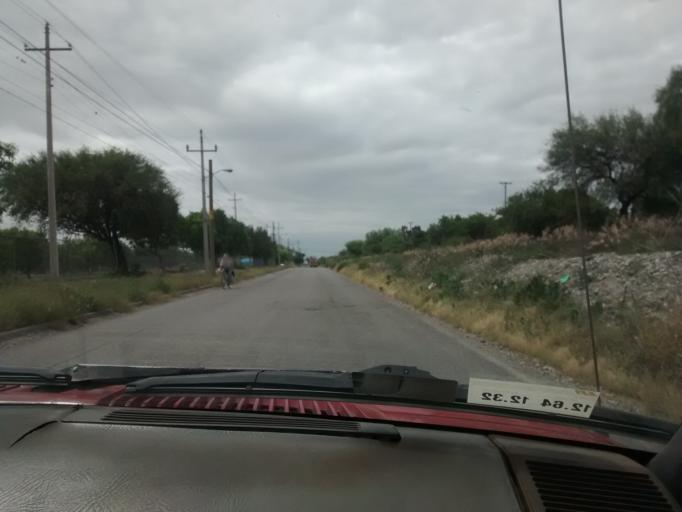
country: MX
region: Puebla
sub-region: Santiago Miahuatlan
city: San Jose Monte Chiquito
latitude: 18.4867
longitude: -97.4158
